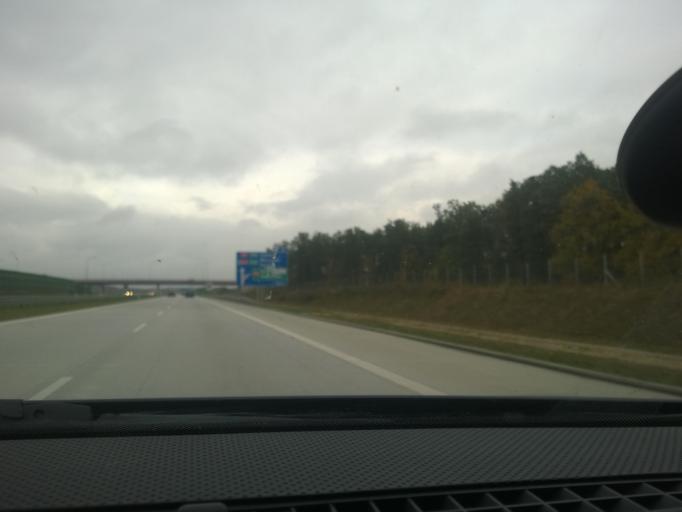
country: PL
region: Lodz Voivodeship
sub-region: Powiat lodzki wschodni
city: Andrespol
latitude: 51.7904
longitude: 19.6168
